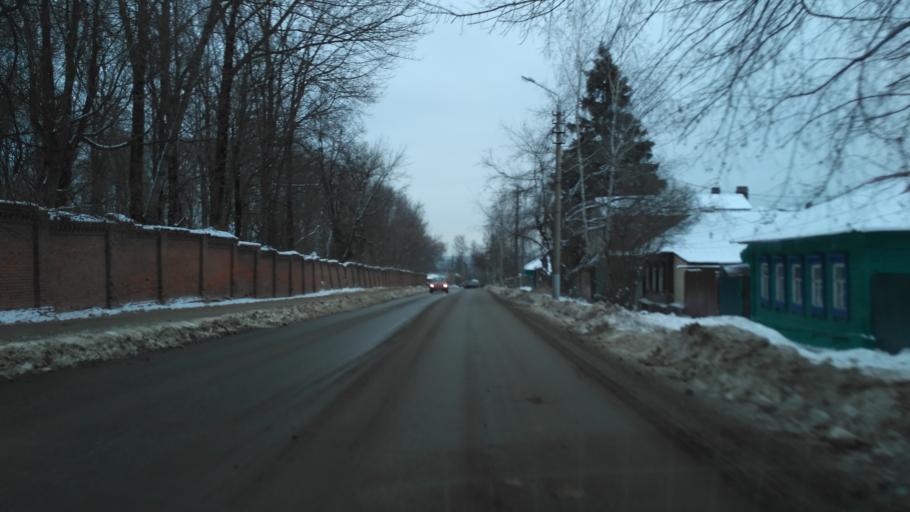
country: RU
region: Tula
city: Tula
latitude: 54.1784
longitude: 37.6152
